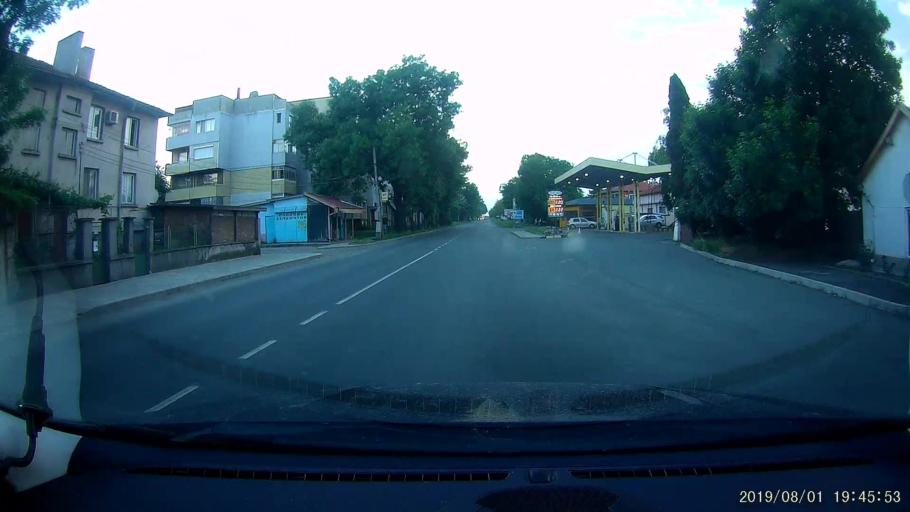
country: BG
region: Burgas
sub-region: Obshtina Karnobat
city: Karnobat
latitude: 42.6509
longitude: 26.9785
